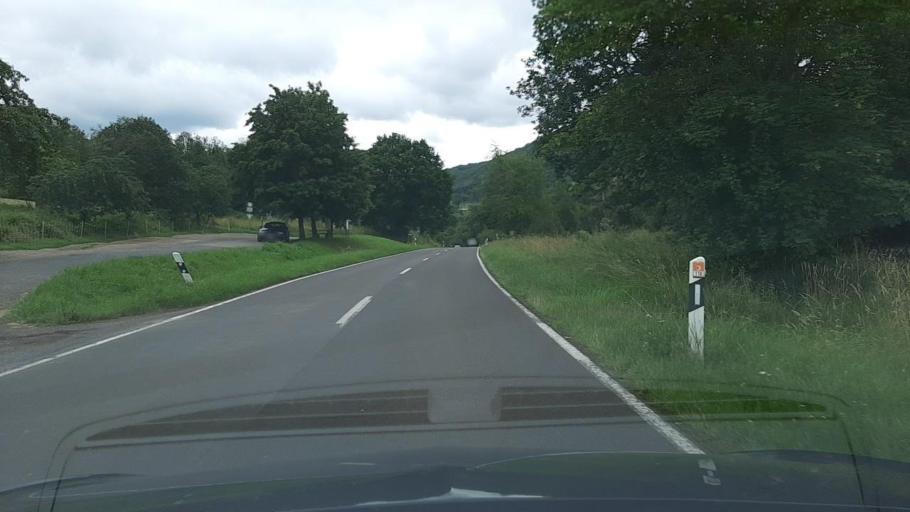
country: DE
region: Rheinland-Pfalz
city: Kamp-Bornhofen
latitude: 50.2071
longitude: 7.6140
